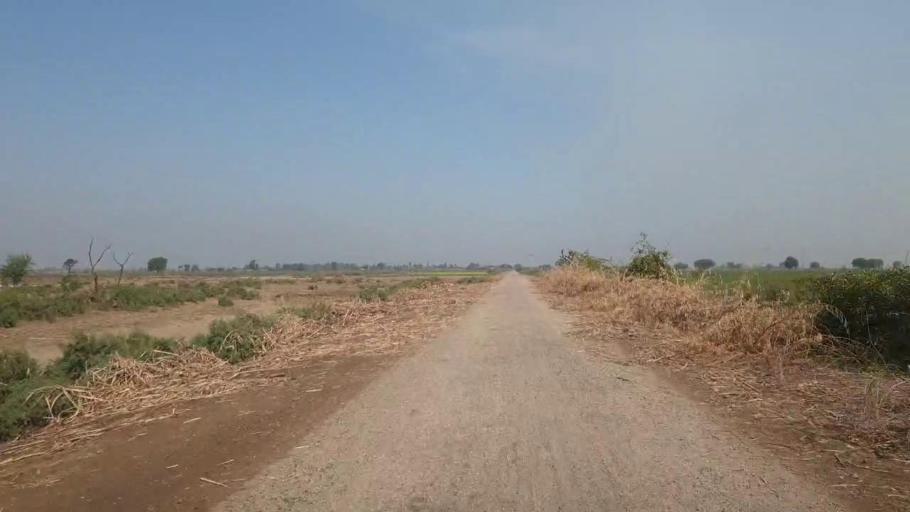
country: PK
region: Sindh
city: Mirwah Gorchani
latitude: 25.3686
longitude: 69.1613
